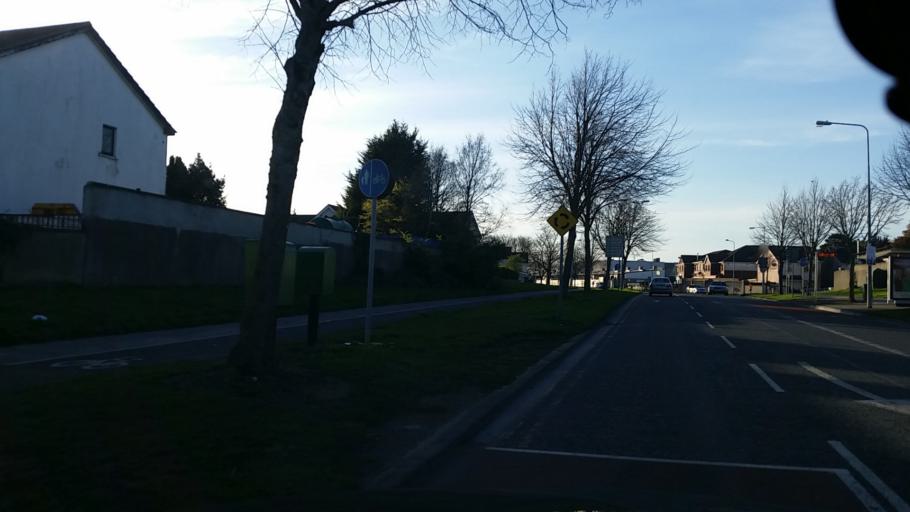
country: IE
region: Leinster
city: Hartstown
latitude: 53.4008
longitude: -6.4060
